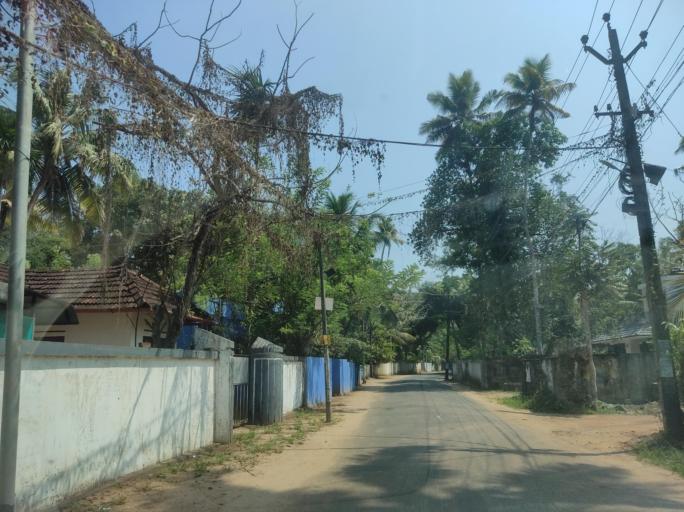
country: IN
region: Kerala
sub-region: Alappuzha
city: Vayalar
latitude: 9.7011
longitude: 76.3033
